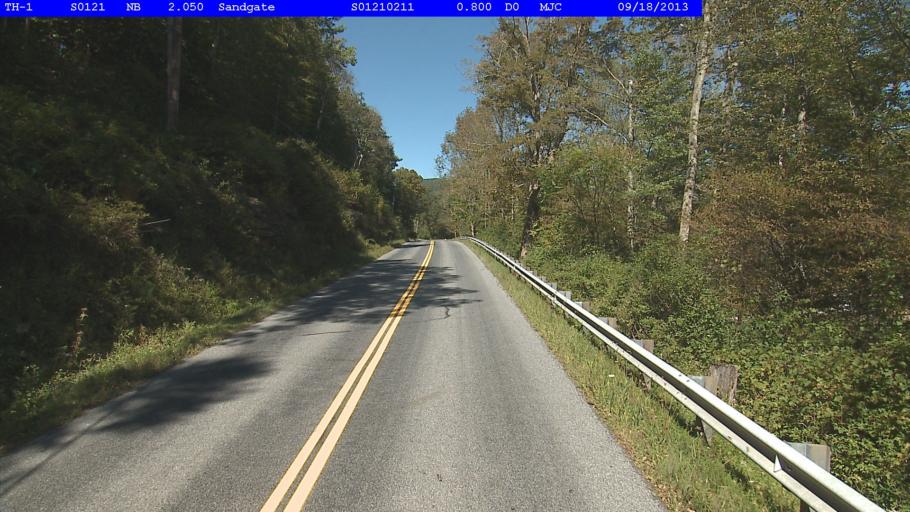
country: US
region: Vermont
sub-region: Bennington County
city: Arlington
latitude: 43.1317
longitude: -73.2045
